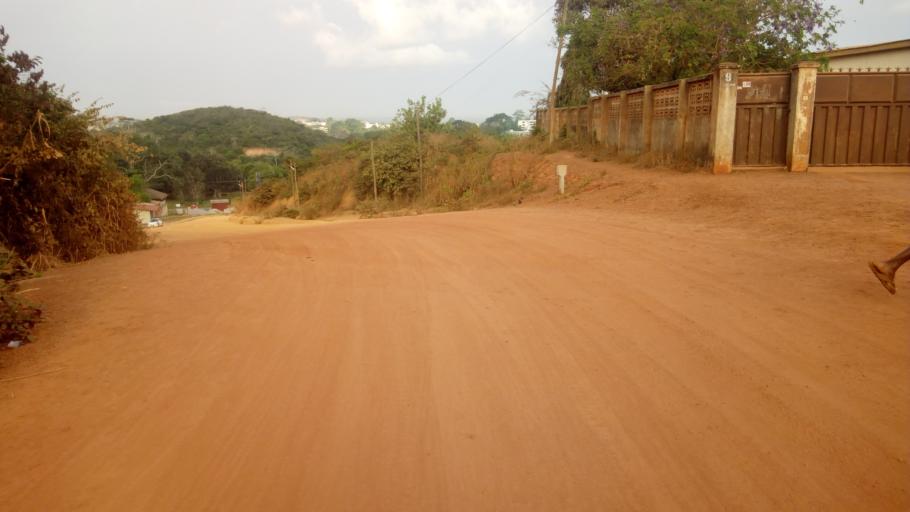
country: GH
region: Central
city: Cape Coast
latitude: 5.1125
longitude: -1.2769
